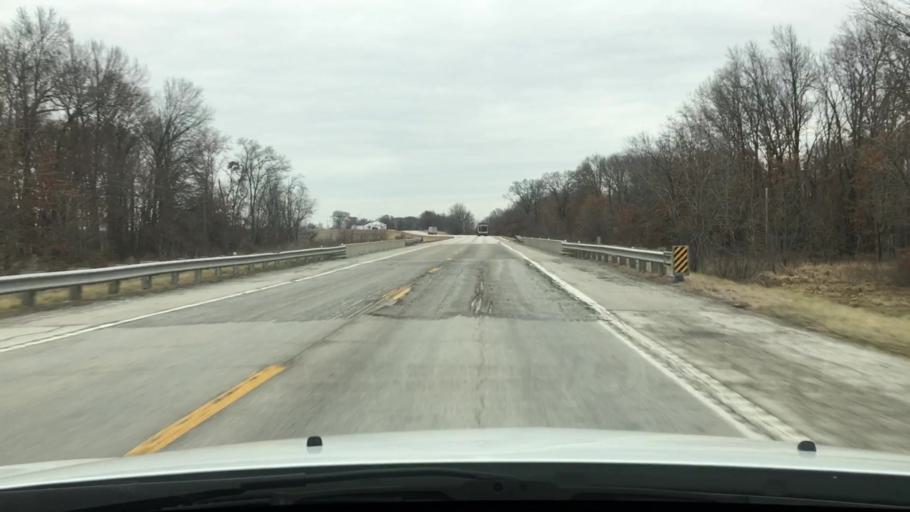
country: US
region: Missouri
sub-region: Montgomery County
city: Wellsville
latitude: 39.1996
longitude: -91.6464
